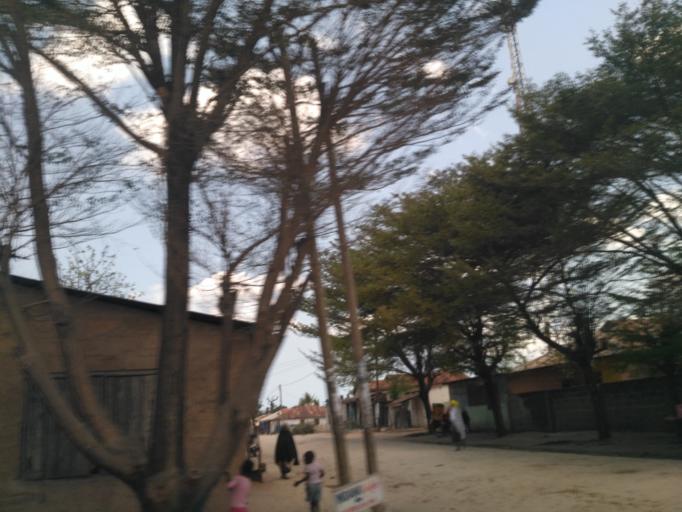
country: TZ
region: Dar es Salaam
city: Dar es Salaam
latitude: -6.8258
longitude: 39.3141
